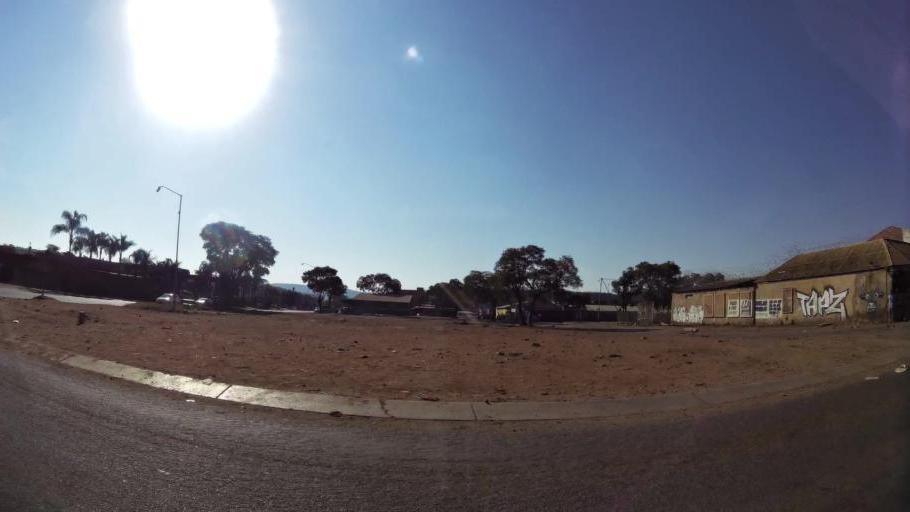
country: ZA
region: Gauteng
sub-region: City of Tshwane Metropolitan Municipality
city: Pretoria
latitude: -25.7416
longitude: 28.1731
